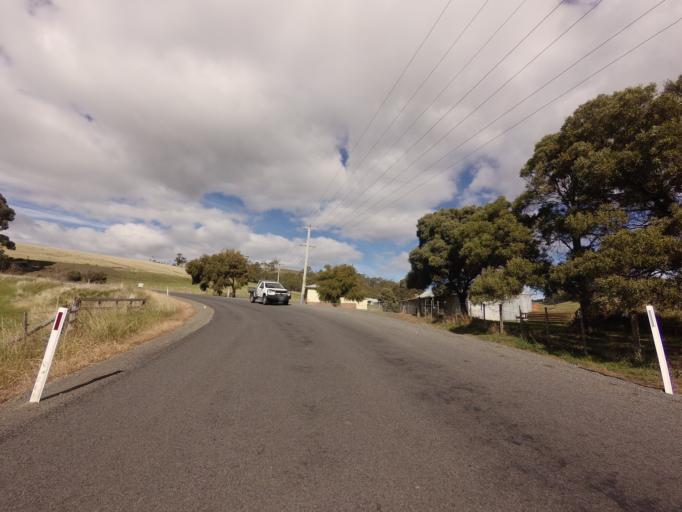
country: AU
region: Tasmania
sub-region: Clarence
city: Sandford
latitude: -43.0383
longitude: 147.7324
